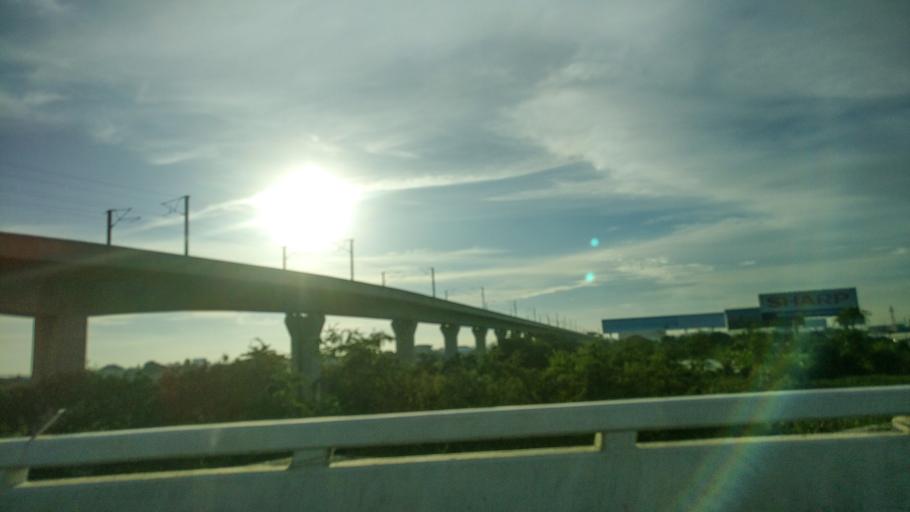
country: TH
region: Bangkok
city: Lat Krabang
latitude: 13.7282
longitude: 100.7594
